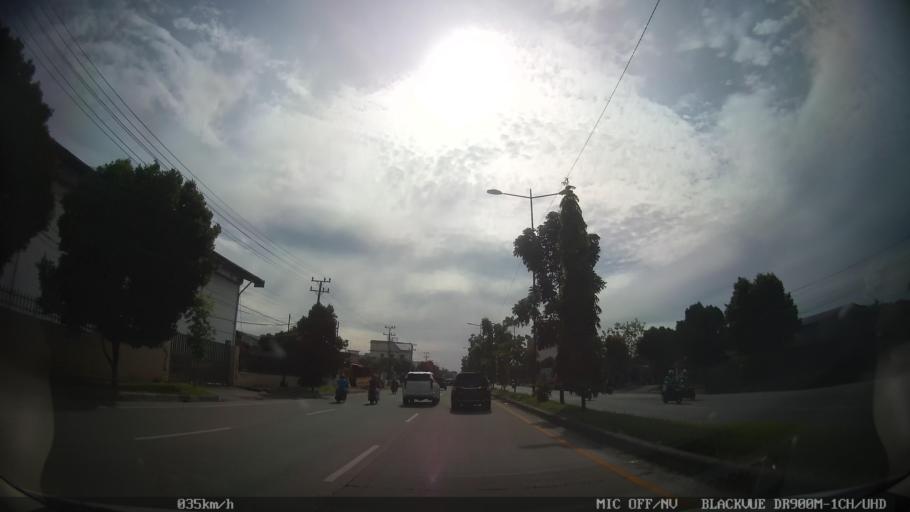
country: ID
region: North Sumatra
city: Medan
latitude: 3.6297
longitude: 98.6829
